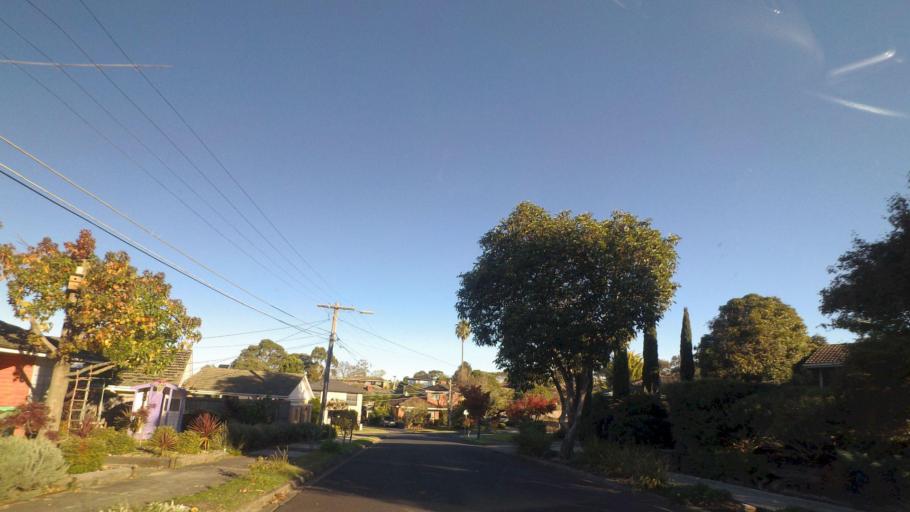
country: AU
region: Victoria
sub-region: Banyule
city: Yallambie
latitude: -37.7301
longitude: 145.0946
